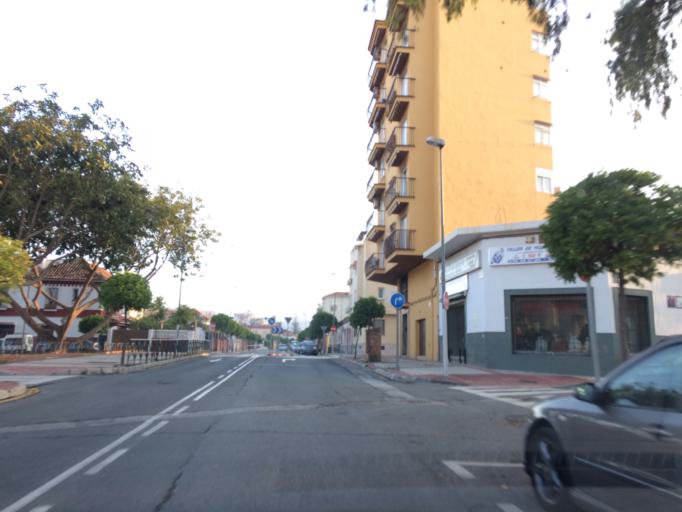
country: ES
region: Andalusia
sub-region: Provincia de Malaga
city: Malaga
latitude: 36.7338
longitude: -4.4238
